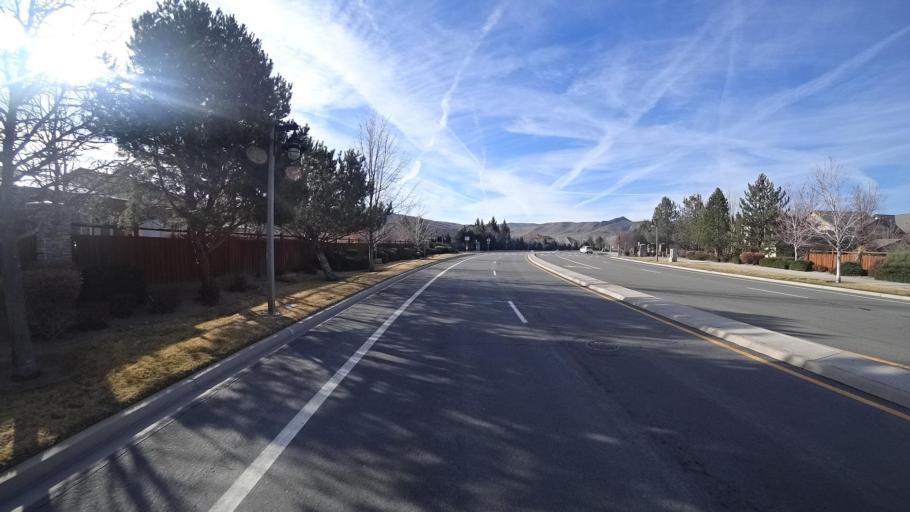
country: US
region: Nevada
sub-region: Washoe County
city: Spanish Springs
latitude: 39.6126
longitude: -119.6692
